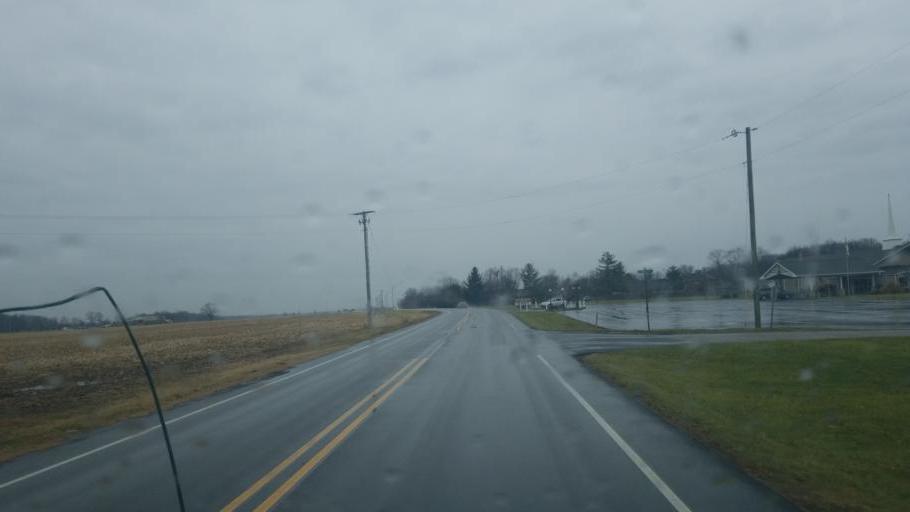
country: US
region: Indiana
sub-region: Shelby County
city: Shelbyville
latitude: 39.4999
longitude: -85.7708
